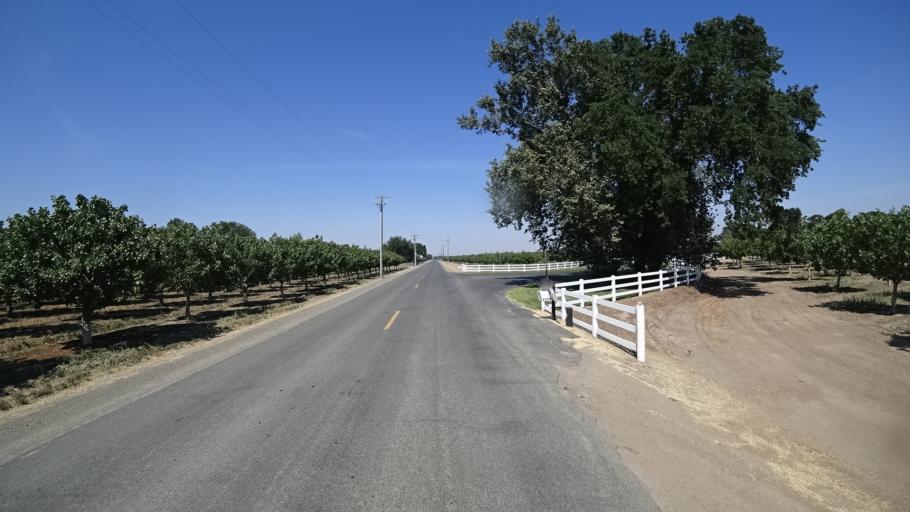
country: US
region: California
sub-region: Kings County
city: Lemoore
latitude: 36.3279
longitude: -119.8242
